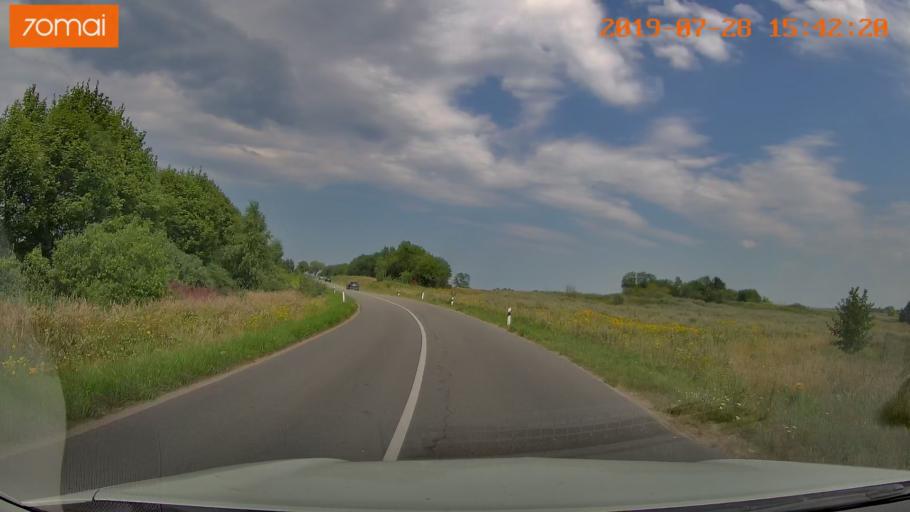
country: RU
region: Kaliningrad
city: Donskoye
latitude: 54.9301
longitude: 20.0092
